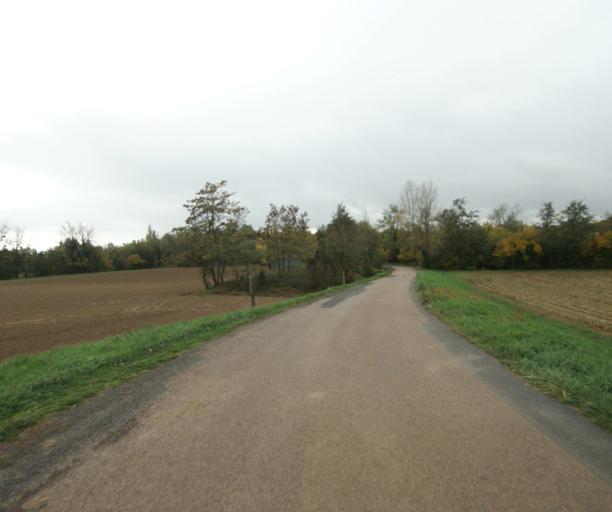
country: FR
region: Rhone-Alpes
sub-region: Departement de l'Ain
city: Pont-de-Vaux
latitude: 46.4757
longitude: 4.8800
